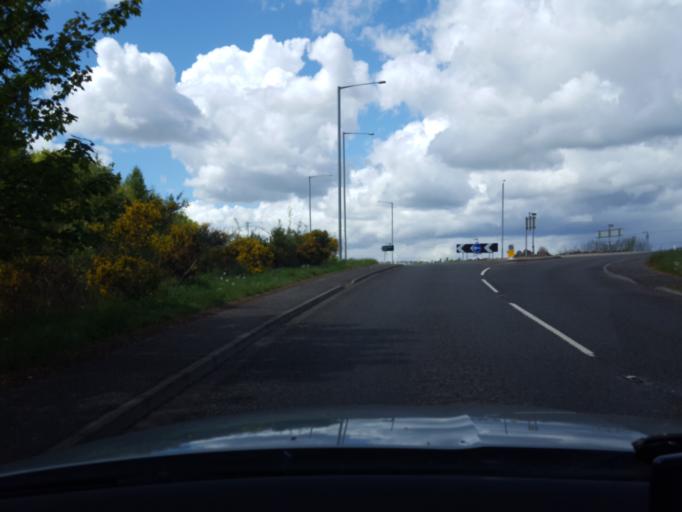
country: GB
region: Scotland
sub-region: Angus
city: Brechin
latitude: 56.7281
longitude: -2.6967
